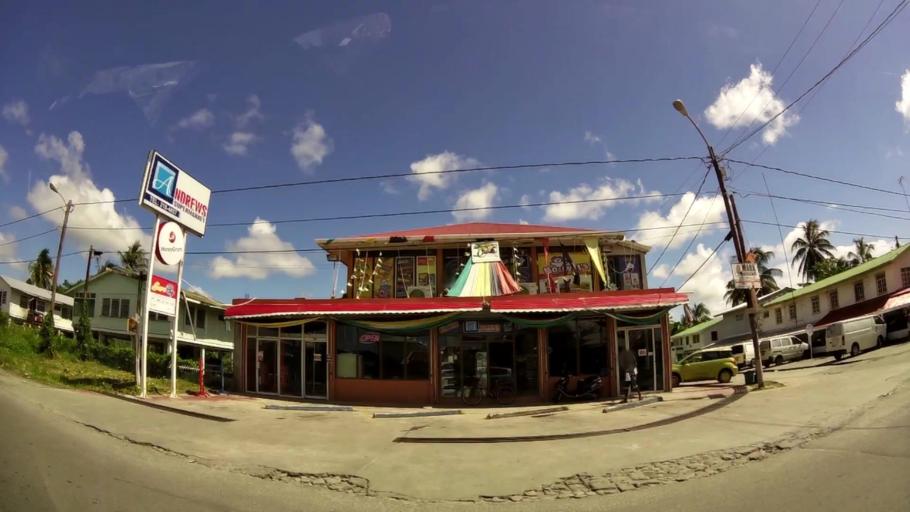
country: GY
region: Demerara-Mahaica
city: Georgetown
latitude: 6.7850
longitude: -58.1355
